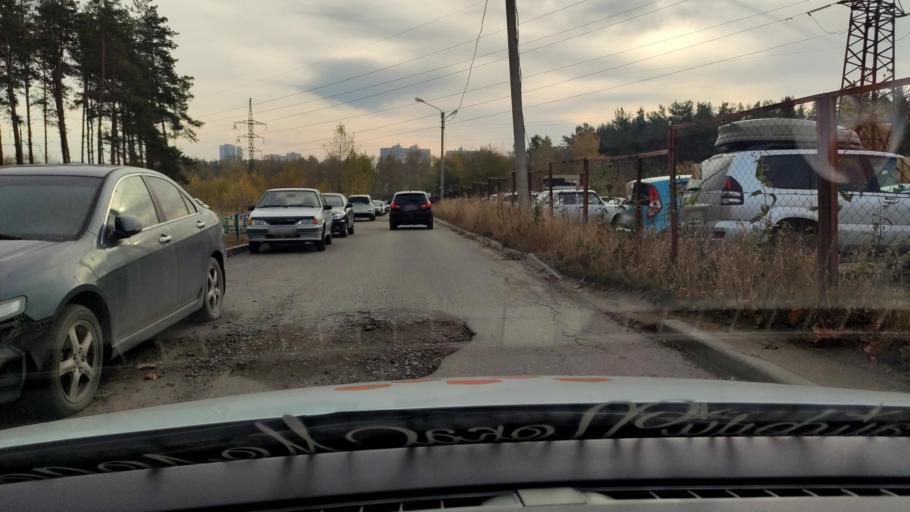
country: RU
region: Voronezj
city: Pridonskoy
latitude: 51.6778
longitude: 39.1230
